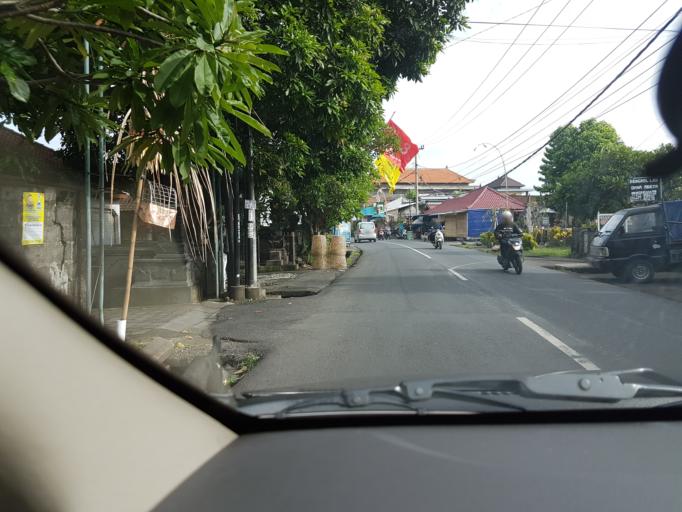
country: ID
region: Bali
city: Denpasar
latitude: -8.6752
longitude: 115.1814
